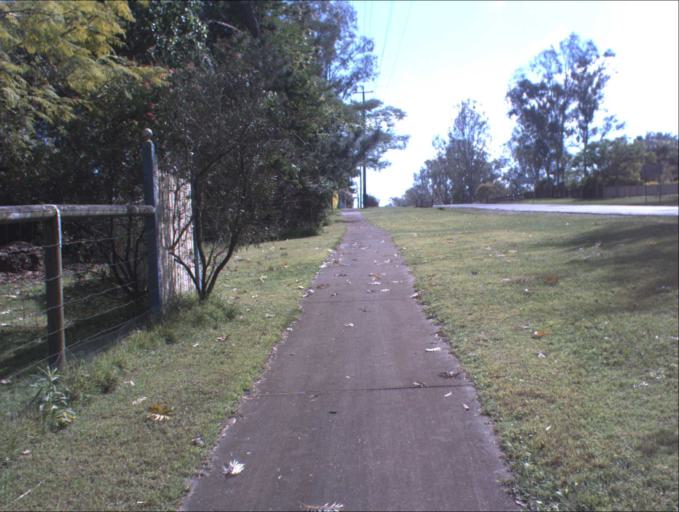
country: AU
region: Queensland
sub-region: Logan
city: Park Ridge South
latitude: -27.7162
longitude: 152.9766
